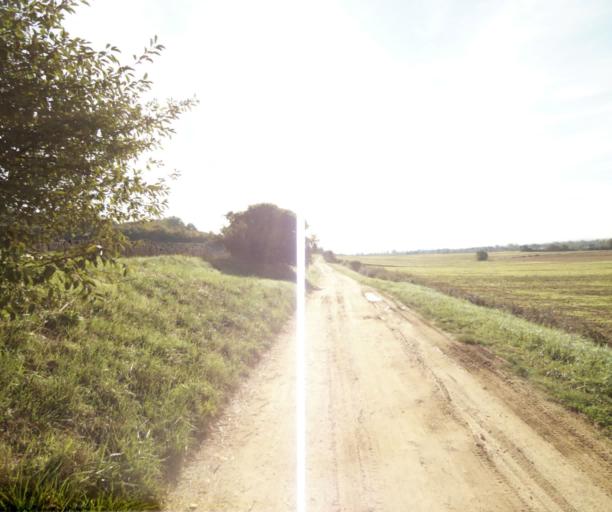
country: FR
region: Midi-Pyrenees
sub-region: Departement du Tarn-et-Garonne
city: Nohic
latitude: 43.9208
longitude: 1.4406
